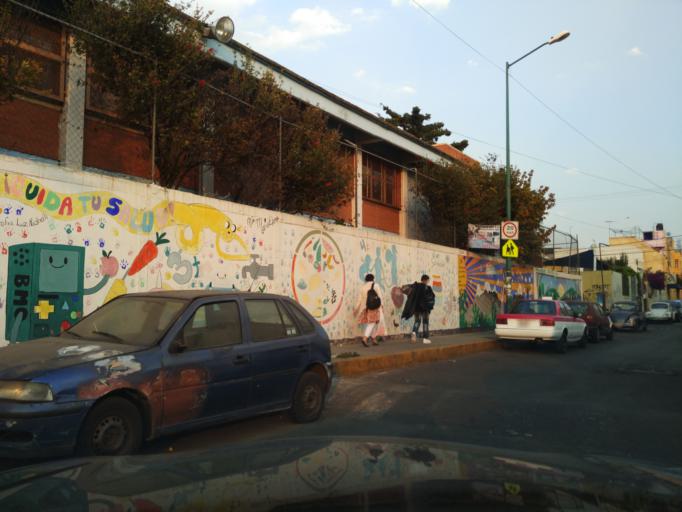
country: MX
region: Mexico City
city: Iztapalapa
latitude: 19.3225
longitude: -99.0865
